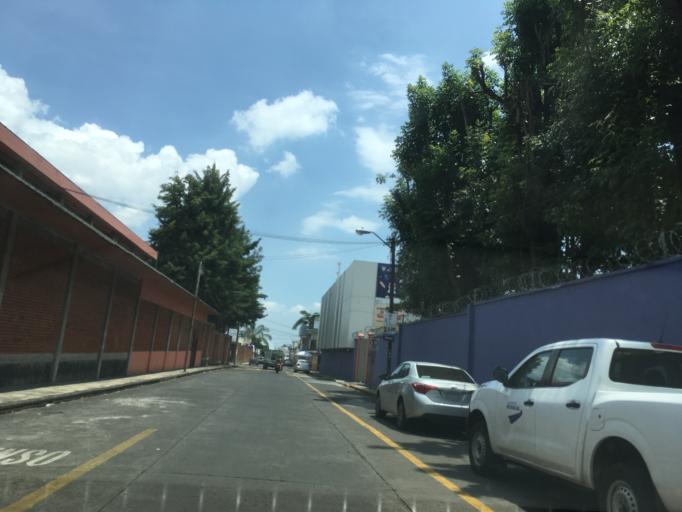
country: MX
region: Michoacan
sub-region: Uruapan
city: Uruapan
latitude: 19.4092
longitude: -102.0554
